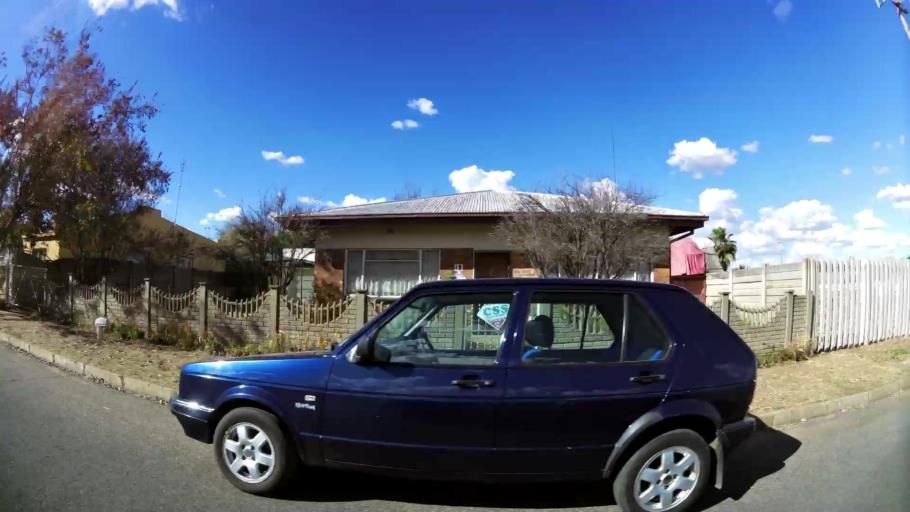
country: ZA
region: North-West
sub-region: Dr Kenneth Kaunda District Municipality
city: Klerksdorp
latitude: -26.8632
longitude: 26.6459
